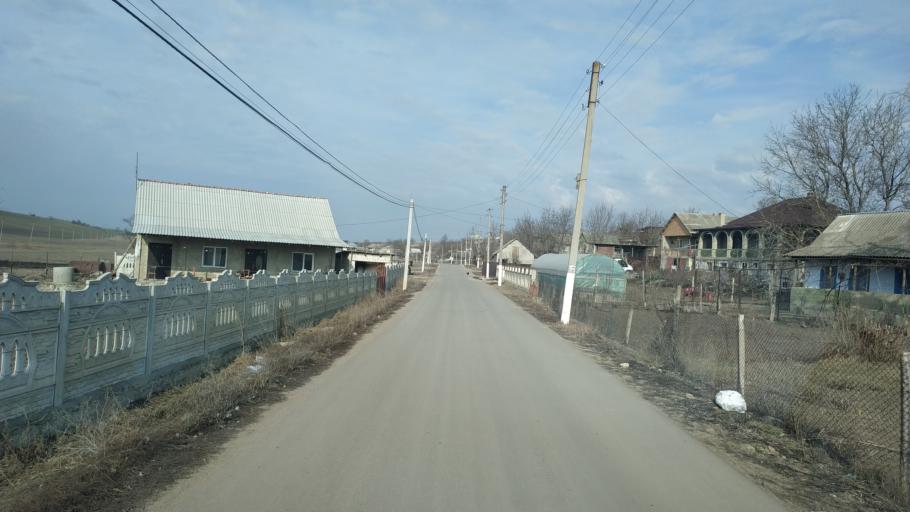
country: MD
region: Chisinau
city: Singera
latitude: 46.9300
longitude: 29.1019
